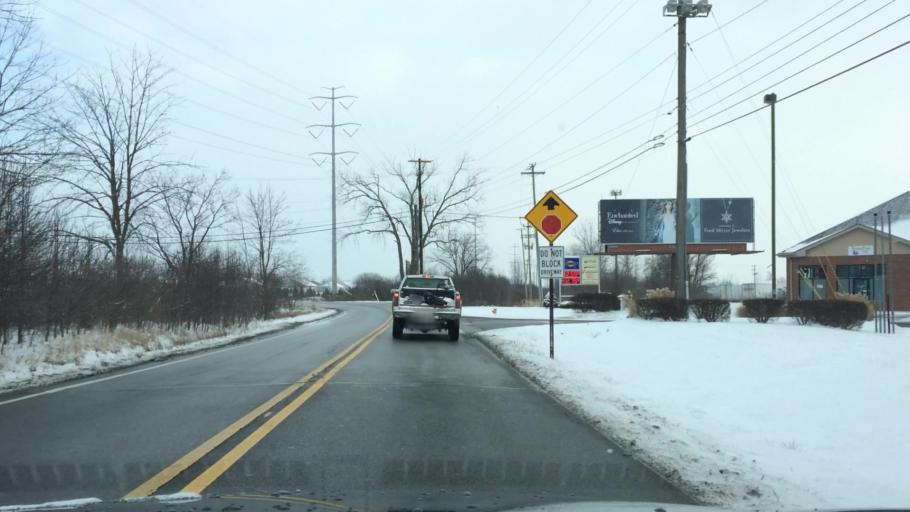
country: US
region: Ohio
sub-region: Franklin County
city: Hilliard
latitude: 40.0184
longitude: -83.1371
